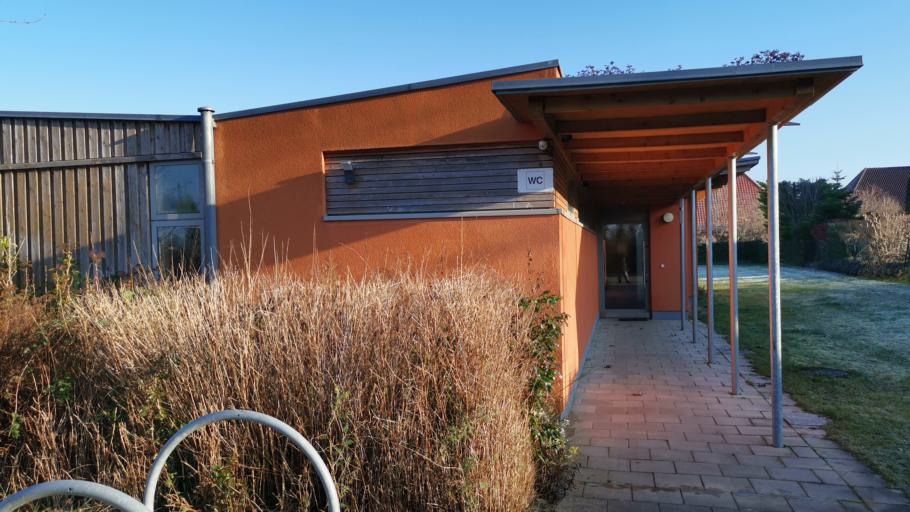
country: DE
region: Schleswig-Holstein
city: Gross Gronau
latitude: 53.7985
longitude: 10.7571
